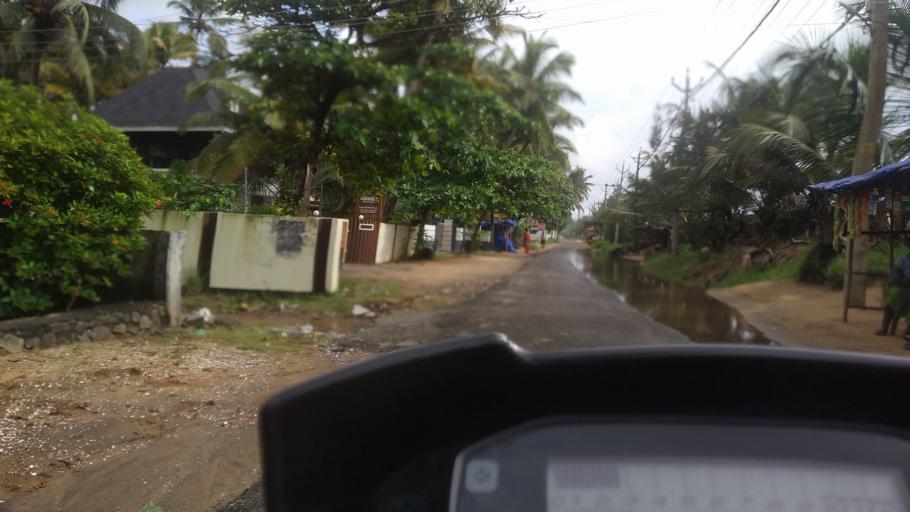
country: IN
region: Kerala
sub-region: Thrissur District
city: Kodungallur
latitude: 10.1334
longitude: 76.1811
